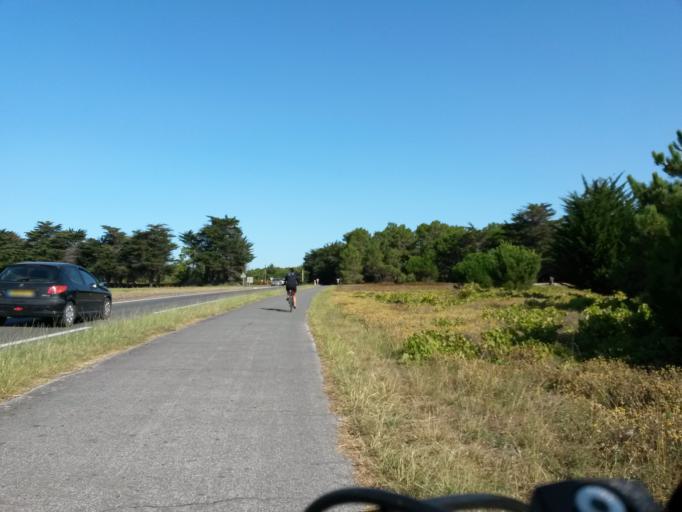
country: FR
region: Poitou-Charentes
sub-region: Departement de la Charente-Maritime
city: Saint-Martin-de-Re
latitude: 46.1691
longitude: -1.3620
